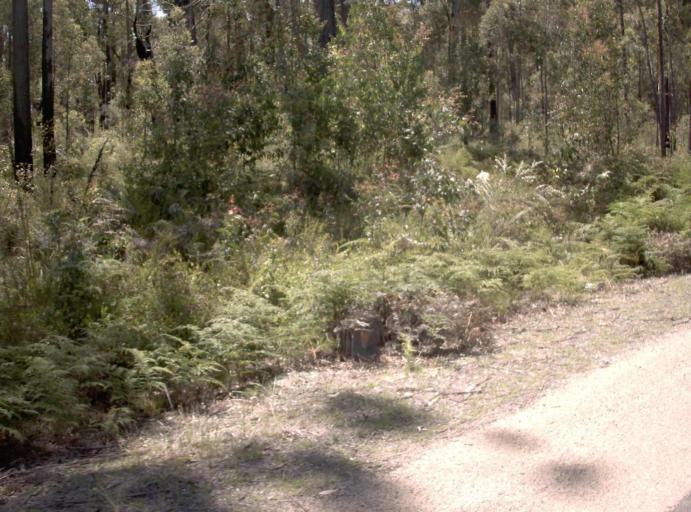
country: AU
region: Victoria
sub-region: East Gippsland
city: Lakes Entrance
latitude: -37.6881
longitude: 148.7508
